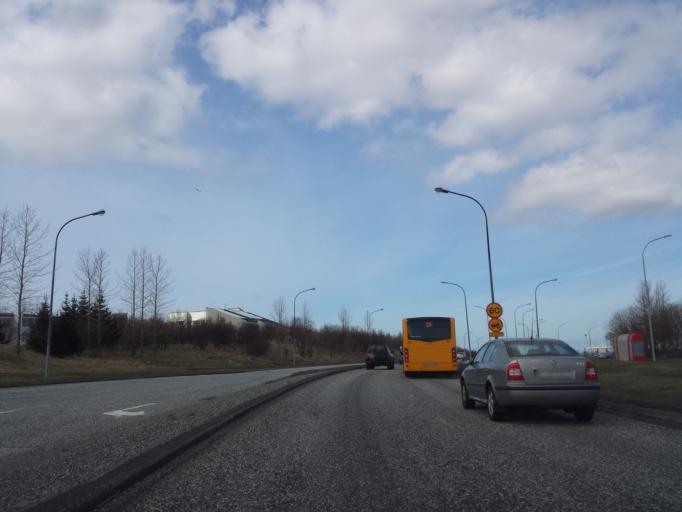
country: IS
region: Capital Region
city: Reykjavik
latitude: 64.0991
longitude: -21.8278
